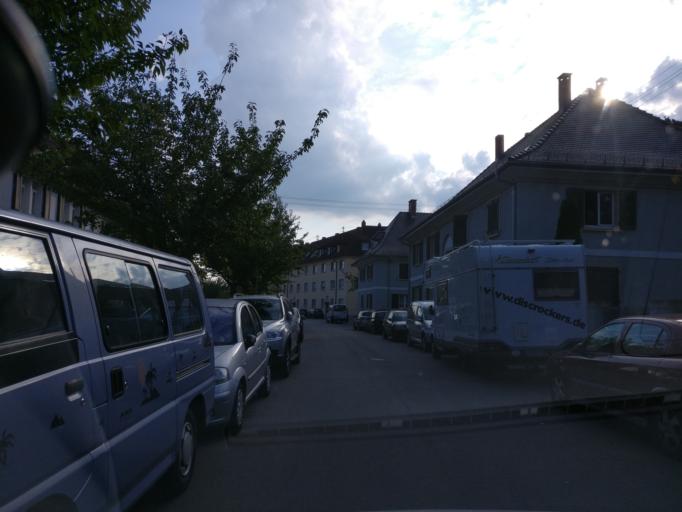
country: DE
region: Baden-Wuerttemberg
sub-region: Karlsruhe Region
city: Karlsruhe
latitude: 48.9943
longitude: 8.4642
